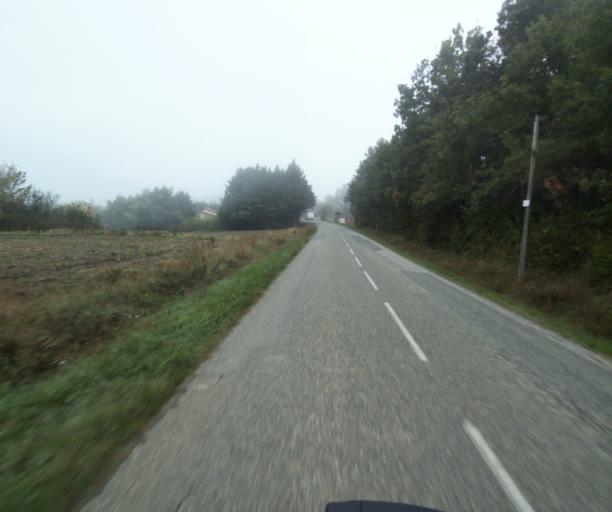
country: FR
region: Midi-Pyrenees
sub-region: Departement du Tarn-et-Garonne
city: Saint-Nauphary
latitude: 43.9393
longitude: 1.4170
